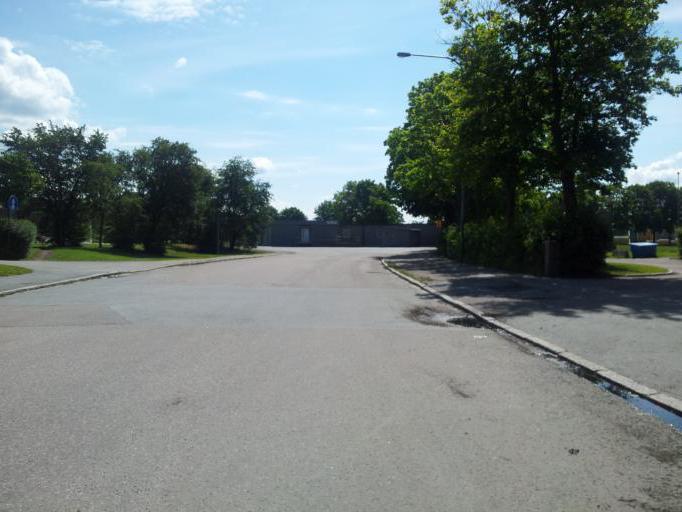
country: SE
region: Uppsala
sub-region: Uppsala Kommun
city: Uppsala
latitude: 59.8639
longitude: 17.6638
